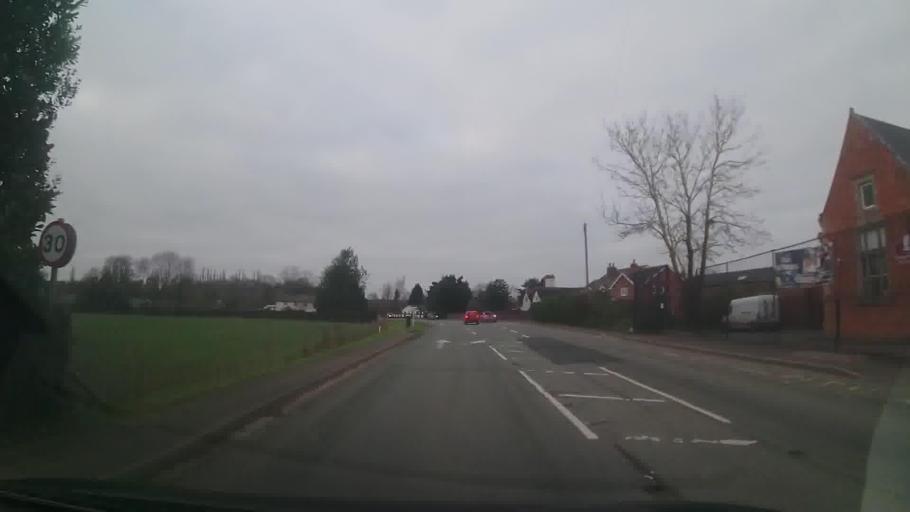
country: GB
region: England
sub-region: Shropshire
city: Bicton
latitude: 52.7262
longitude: -2.8182
